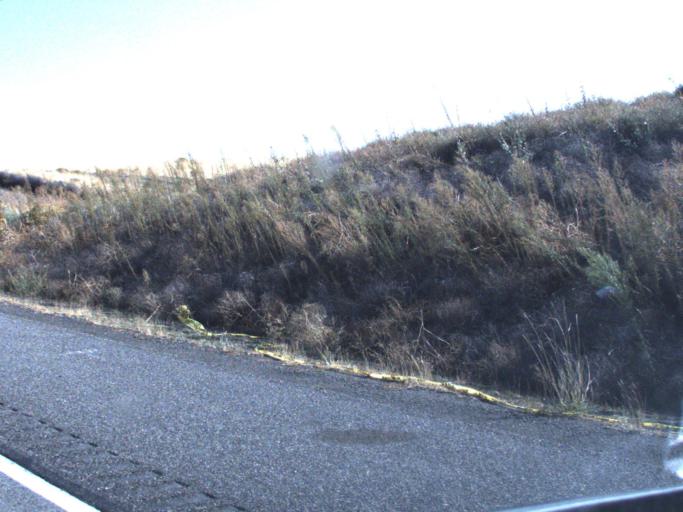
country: US
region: Washington
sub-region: Franklin County
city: West Pasco
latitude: 46.1806
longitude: -119.2408
